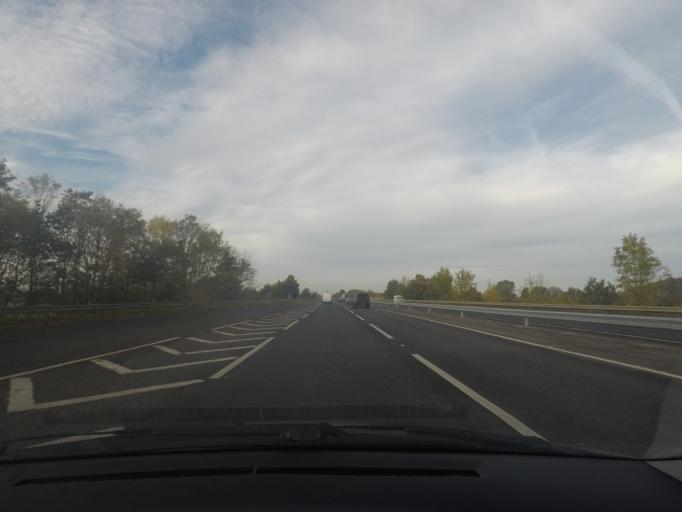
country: GB
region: England
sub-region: City of York
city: Copmanthorpe
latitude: 53.9235
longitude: -1.1233
